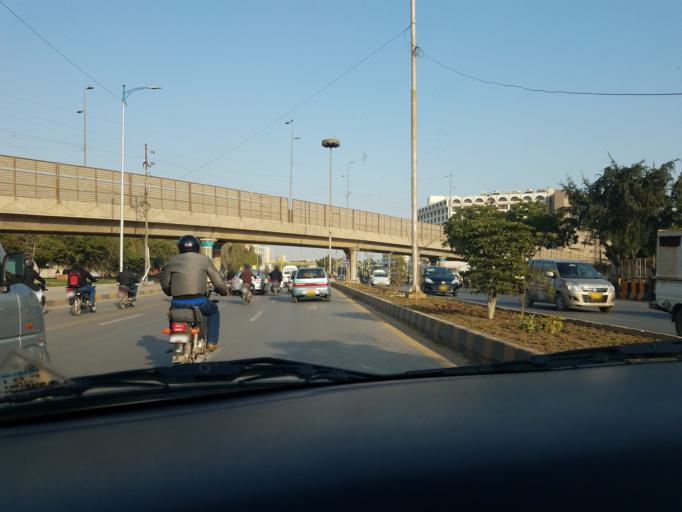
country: PK
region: Sindh
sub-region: Karachi District
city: Karachi
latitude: 24.8552
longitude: 67.0374
